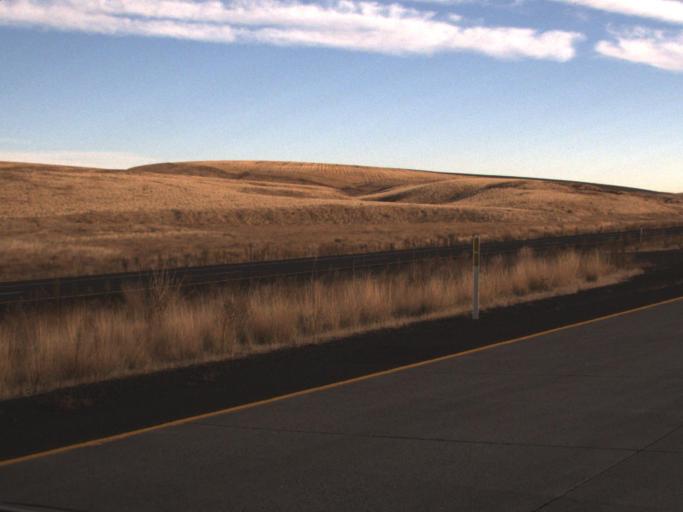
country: US
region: Washington
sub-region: Franklin County
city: Connell
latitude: 46.8383
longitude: -118.6487
